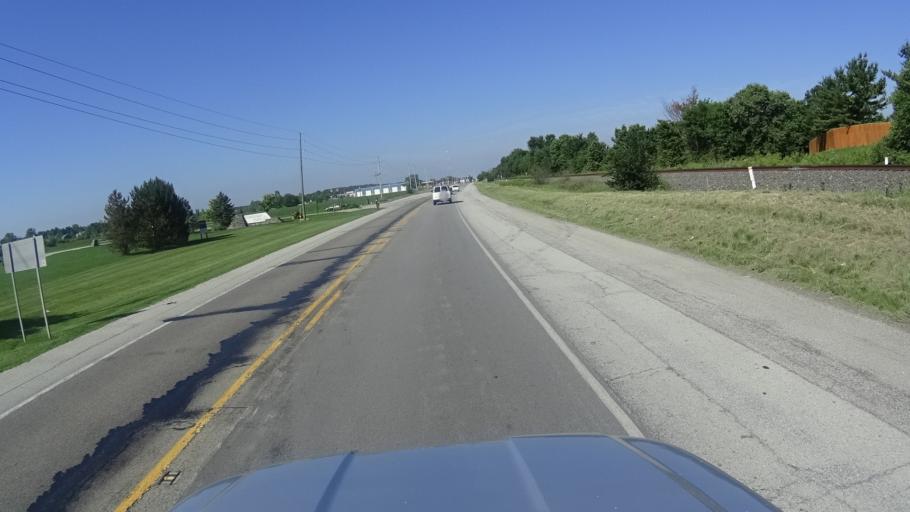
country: US
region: Indiana
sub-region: Madison County
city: Pendleton
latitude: 39.9868
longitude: -85.7454
